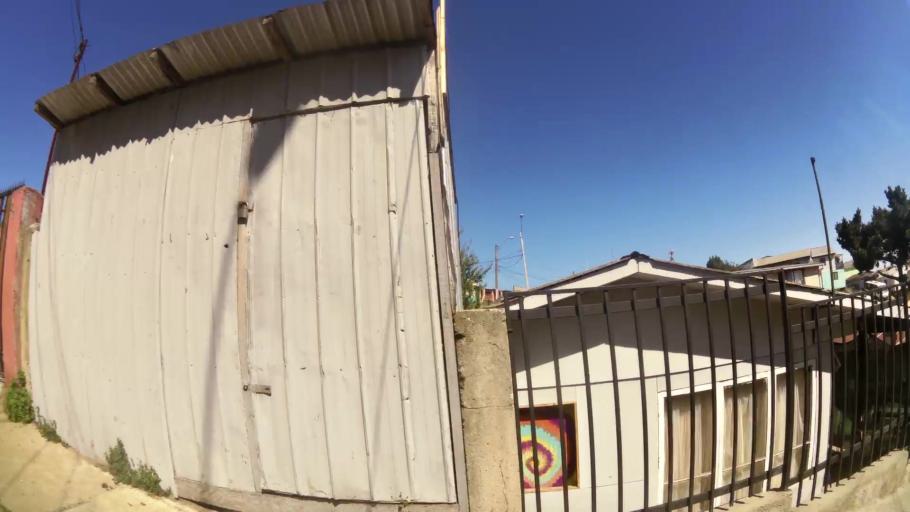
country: CL
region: Valparaiso
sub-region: Provincia de Valparaiso
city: Valparaiso
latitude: -33.0516
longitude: -71.6455
